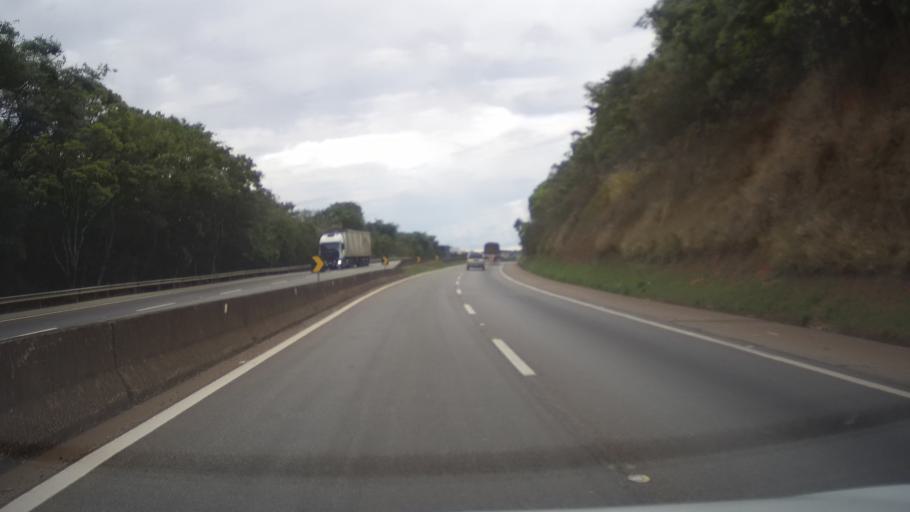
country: BR
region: Minas Gerais
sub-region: Itauna
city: Itauna
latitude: -20.3361
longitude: -44.4457
